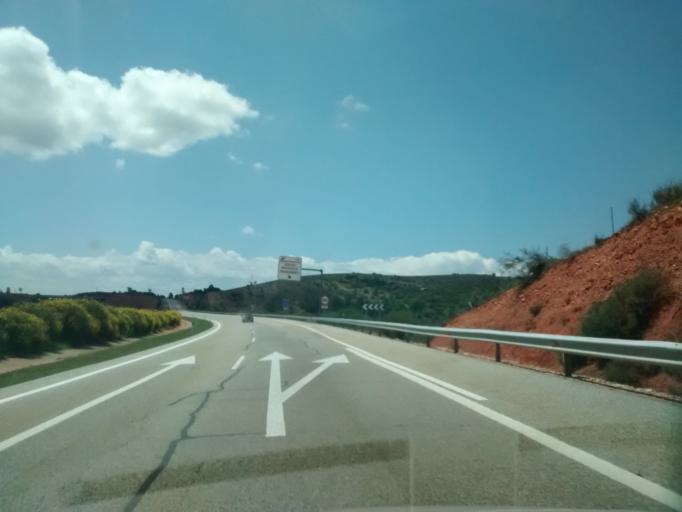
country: ES
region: Castille and Leon
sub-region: Provincia de Leon
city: Brazuelo
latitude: 42.4968
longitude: -6.1269
